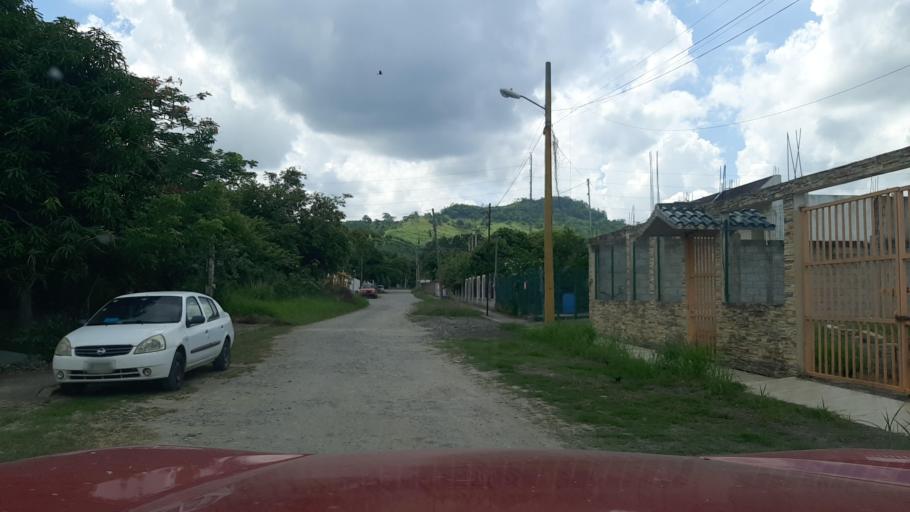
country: MX
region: Veracruz
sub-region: Poza Rica de Hidalgo
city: Villa de las Flores
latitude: 20.5714
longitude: -97.4347
